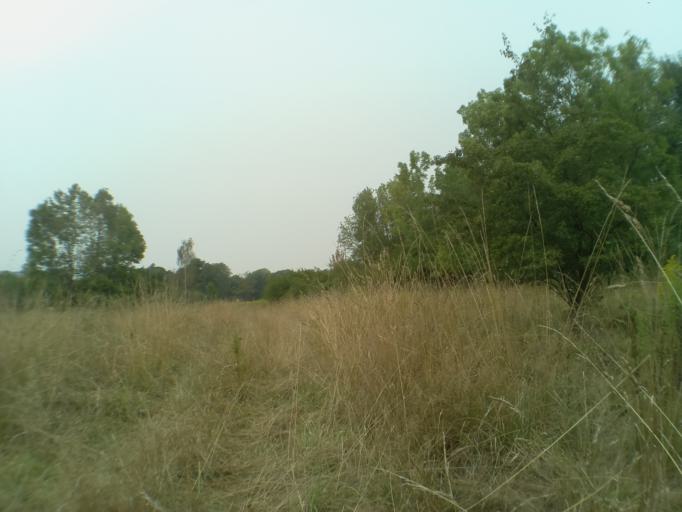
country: PL
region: Lower Silesian Voivodeship
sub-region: Powiat swidnicki
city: Strzegom
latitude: 50.9979
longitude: 16.2722
